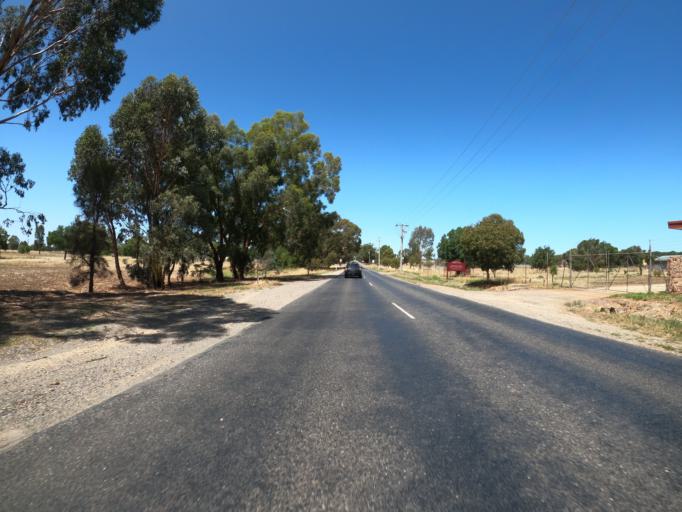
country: AU
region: New South Wales
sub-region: Corowa Shire
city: Corowa
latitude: -36.0126
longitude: 146.4014
